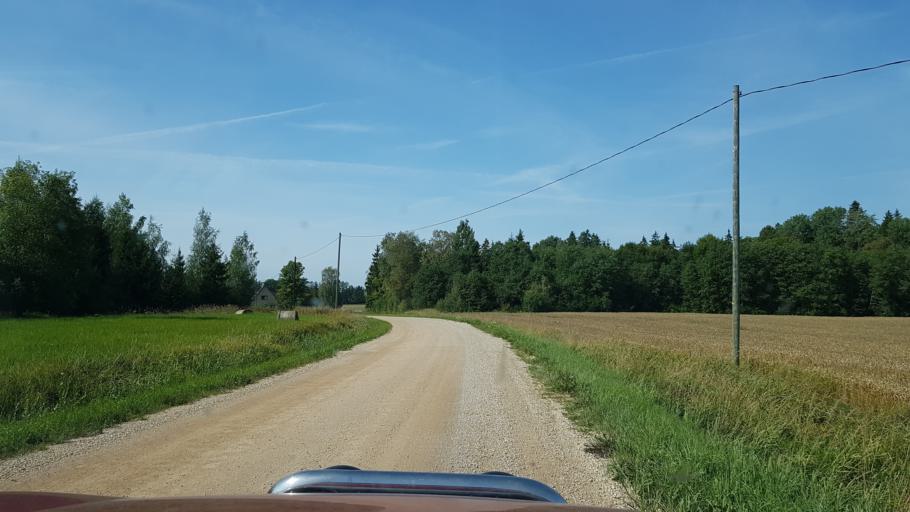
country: EE
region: Viljandimaa
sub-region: Viljandi linn
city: Viljandi
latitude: 58.4056
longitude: 25.5311
